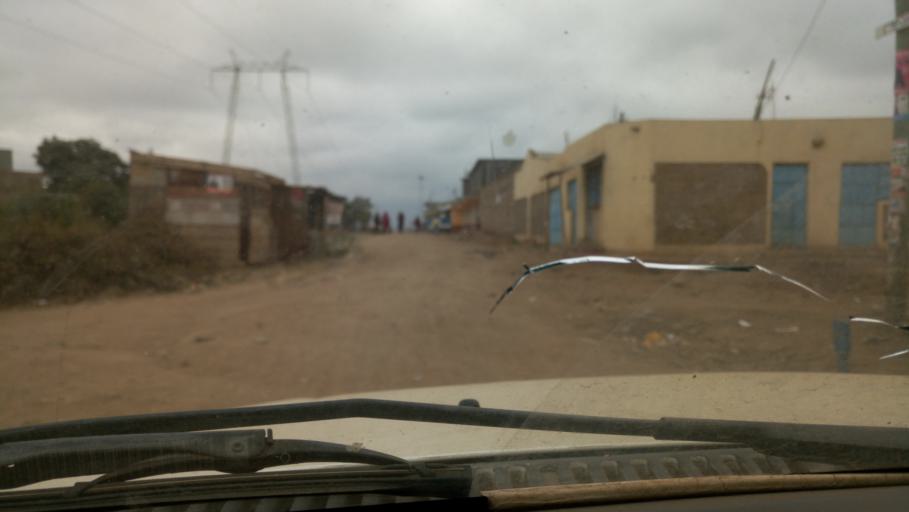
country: KE
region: Nairobi Area
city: Pumwani
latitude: -1.2537
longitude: 36.9185
